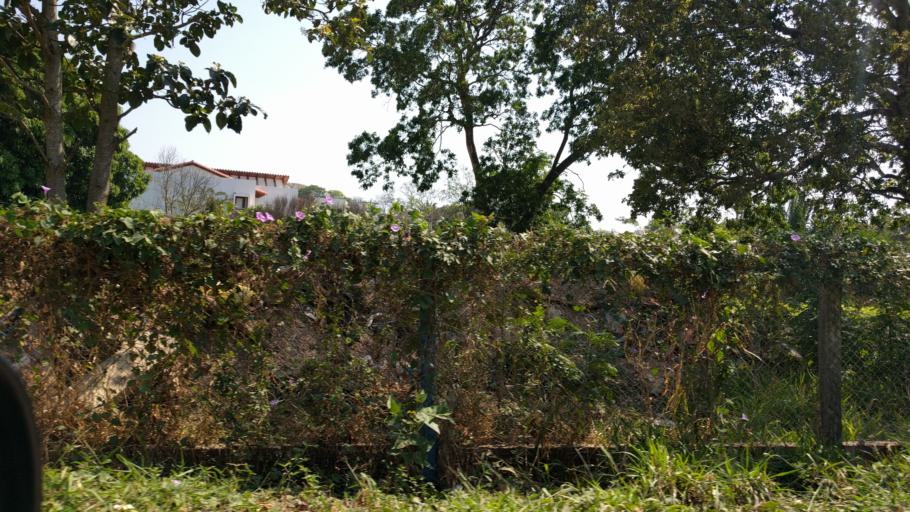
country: BO
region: Santa Cruz
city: Santa Cruz de la Sierra
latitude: -17.7538
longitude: -63.2250
